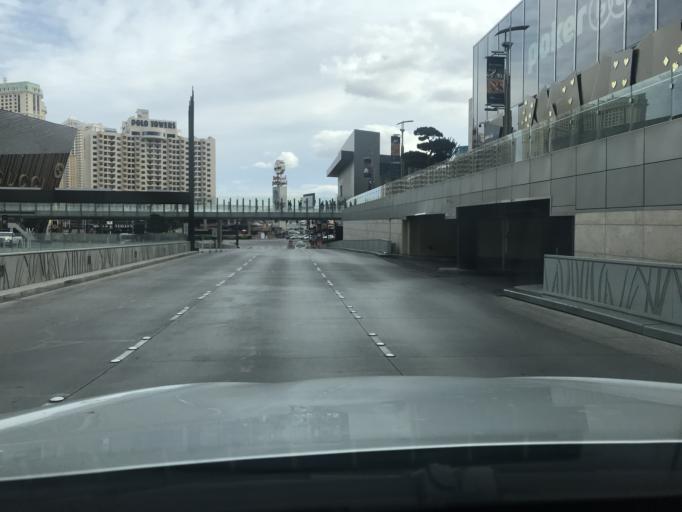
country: US
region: Nevada
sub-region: Clark County
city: Paradise
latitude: 36.1070
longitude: -115.1750
